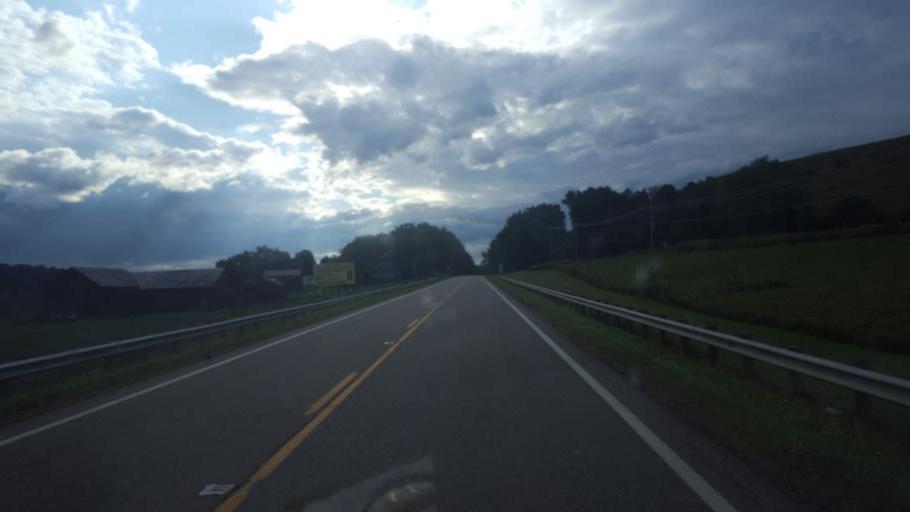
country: US
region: Ohio
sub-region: Holmes County
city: Millersburg
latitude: 40.4815
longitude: -82.0122
